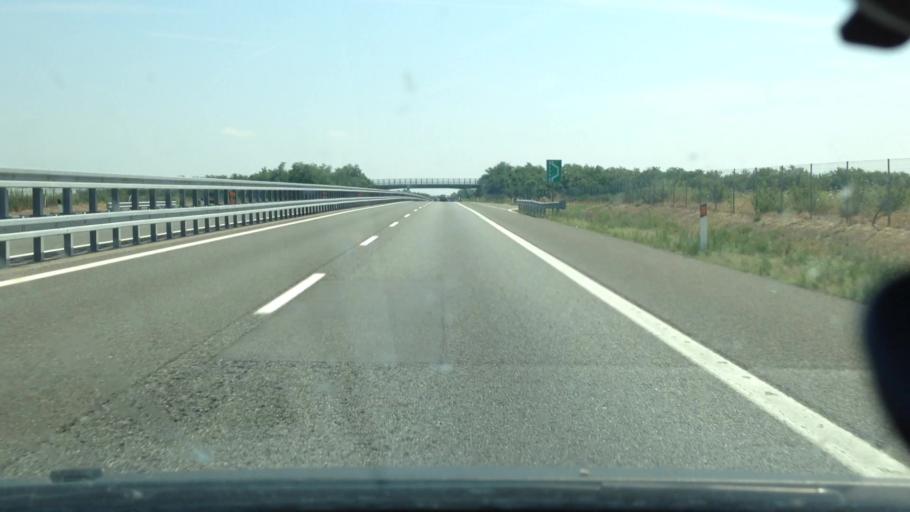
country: IT
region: Piedmont
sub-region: Provincia di Alessandria
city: Felizzano
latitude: 44.9172
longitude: 8.4460
